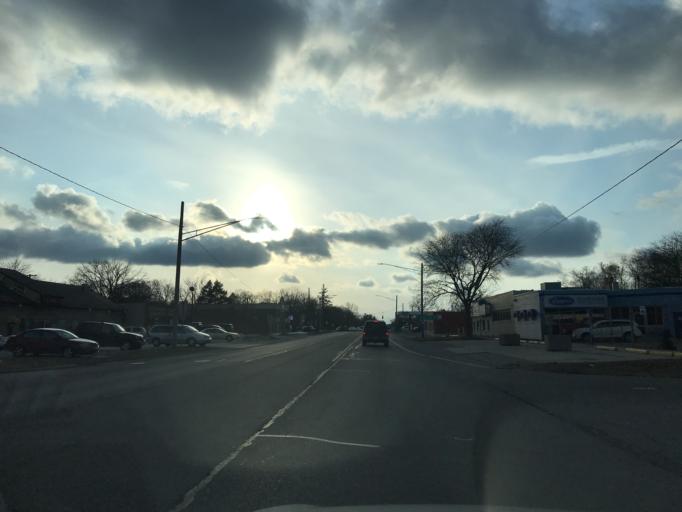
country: US
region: Michigan
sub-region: Wayne County
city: Redford
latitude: 42.4277
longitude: -83.3135
